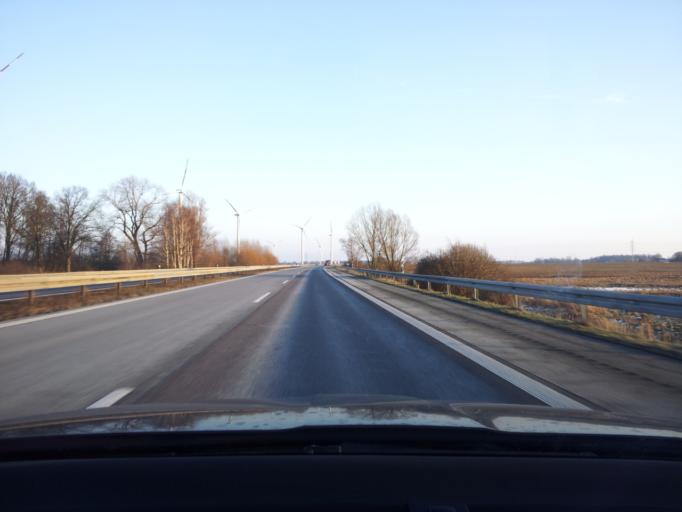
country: DE
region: Brandenburg
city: Walsleben
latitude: 52.9362
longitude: 12.6911
